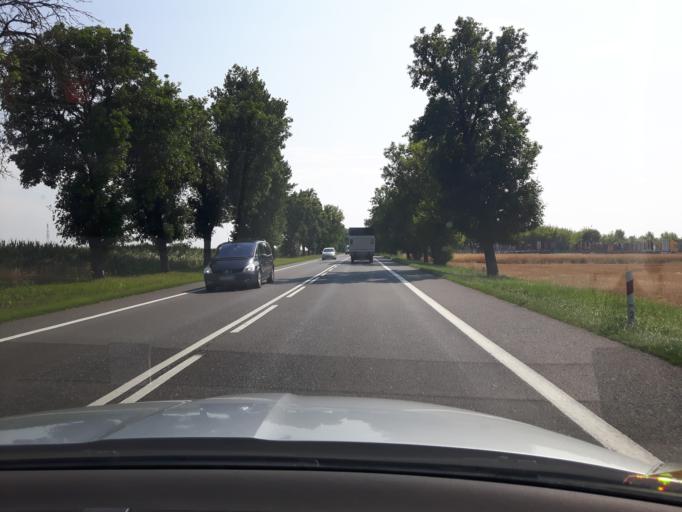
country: PL
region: Masovian Voivodeship
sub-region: Powiat mlawski
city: Wisniewo
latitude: 53.0254
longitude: 20.3360
